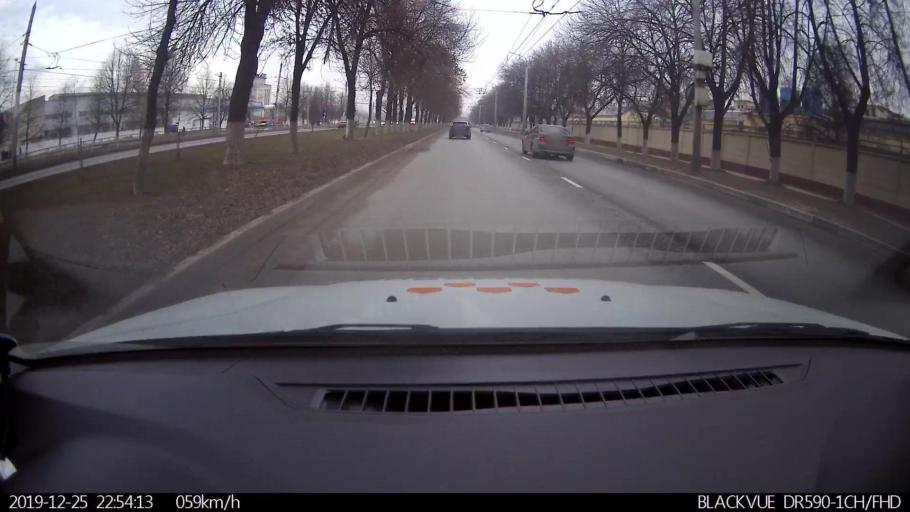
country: RU
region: Nizjnij Novgorod
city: Nizhniy Novgorod
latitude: 56.2546
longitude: 43.8970
